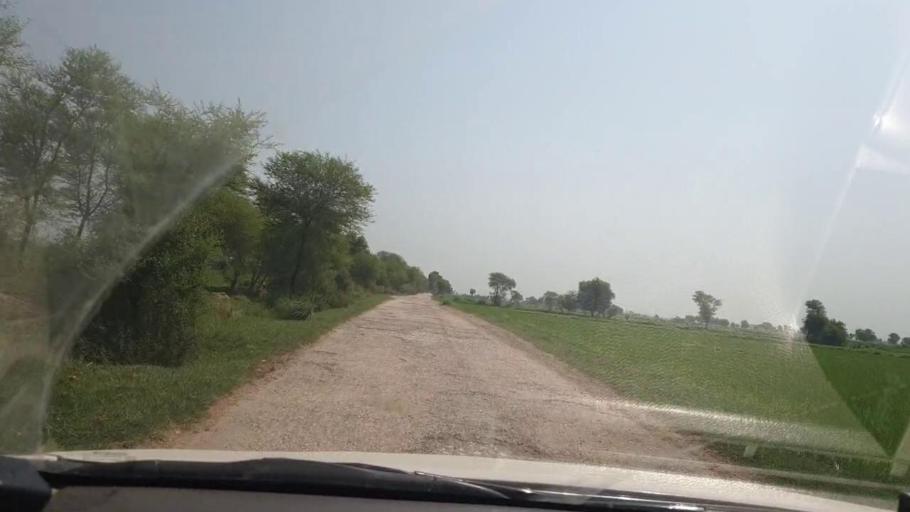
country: PK
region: Sindh
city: Chak
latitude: 27.8894
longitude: 68.7855
